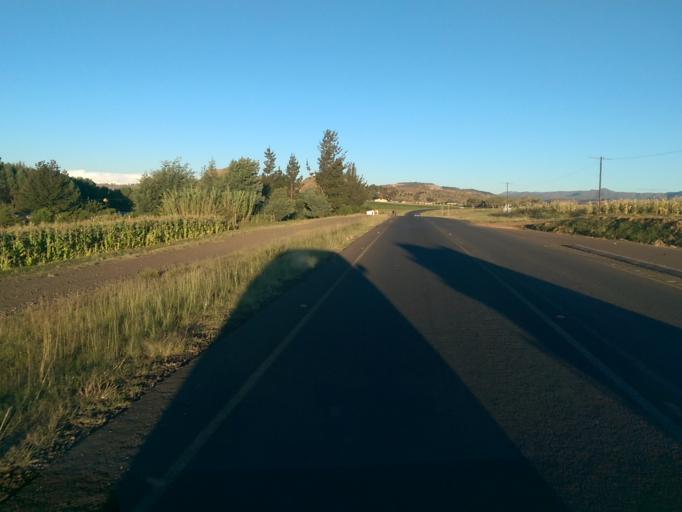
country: LS
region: Maseru
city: Maseru
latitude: -29.4080
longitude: 27.6021
